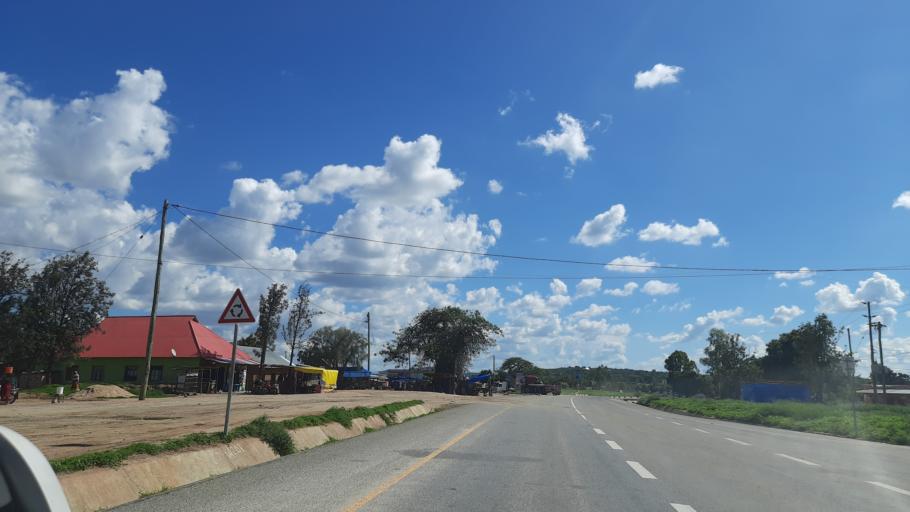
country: TZ
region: Dodoma
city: Kondoa
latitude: -4.9162
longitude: 35.8104
